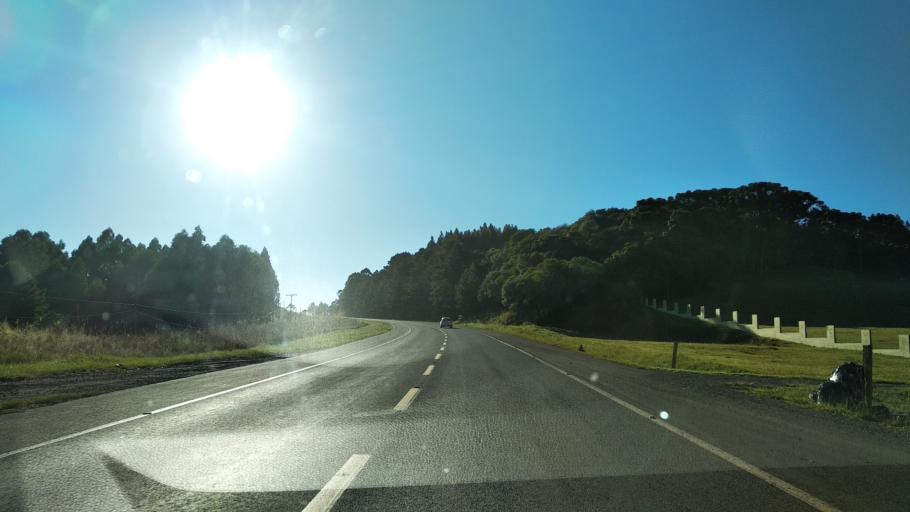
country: BR
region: Santa Catarina
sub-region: Lages
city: Lages
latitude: -27.7953
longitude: -50.3842
